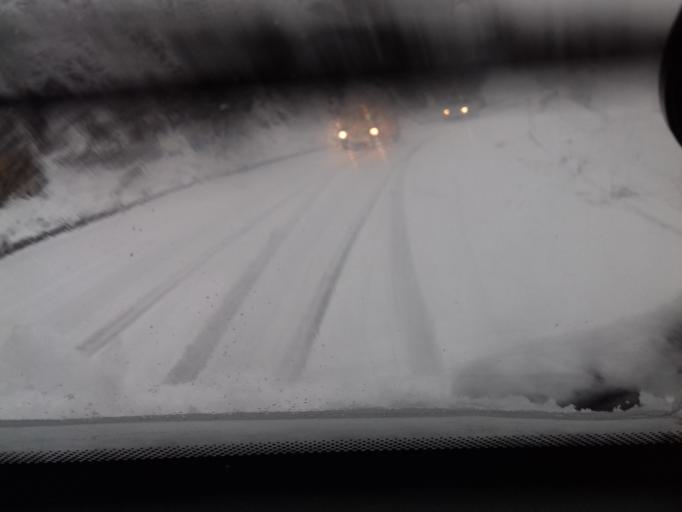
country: BA
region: Federation of Bosnia and Herzegovina
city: Lokvine
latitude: 44.2387
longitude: 17.8186
